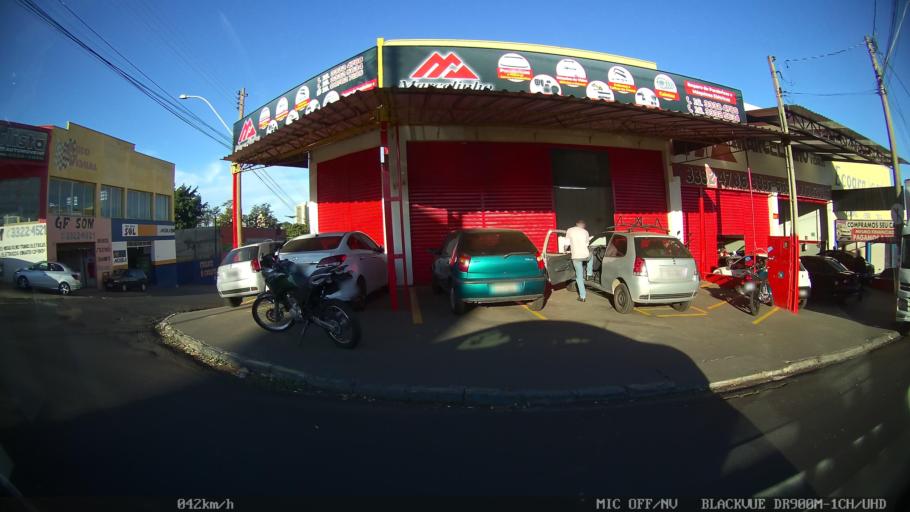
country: BR
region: Sao Paulo
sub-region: Araraquara
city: Araraquara
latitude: -21.8073
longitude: -48.1764
